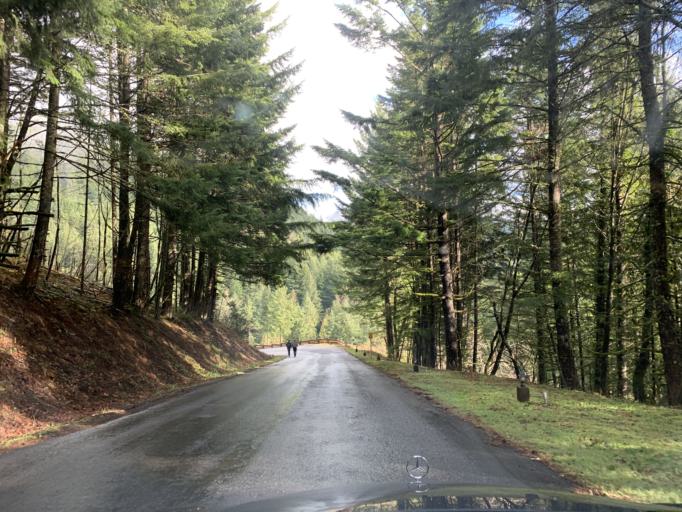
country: US
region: Washington
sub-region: Skamania County
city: Carson
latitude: 45.7269
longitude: -121.7980
